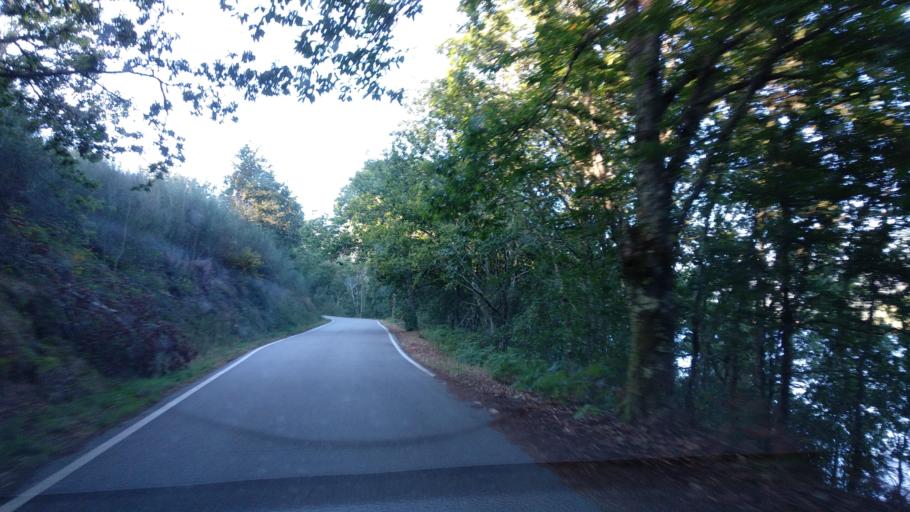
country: ES
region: Galicia
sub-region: Provincia de Pontevedra
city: Fornelos de Montes
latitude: 42.3481
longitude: -8.4889
